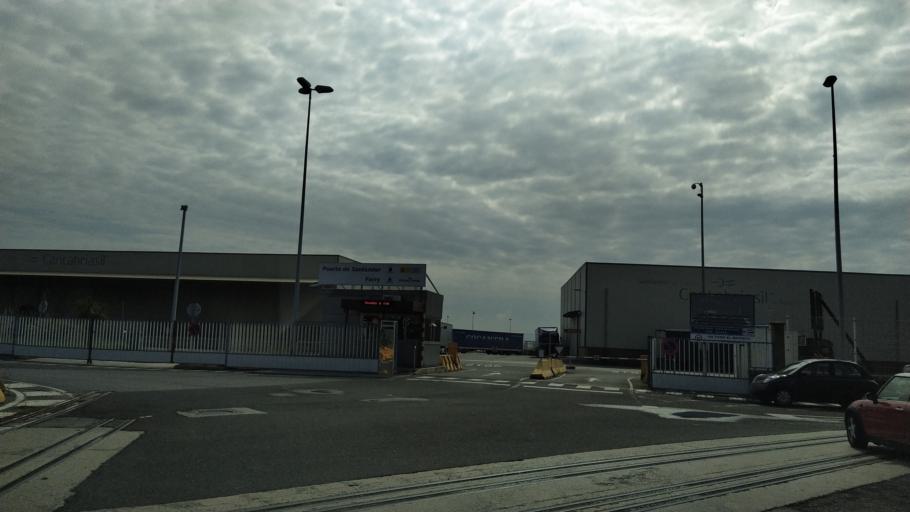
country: ES
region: Cantabria
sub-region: Provincia de Cantabria
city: Santander
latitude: 43.4531
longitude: -3.8141
